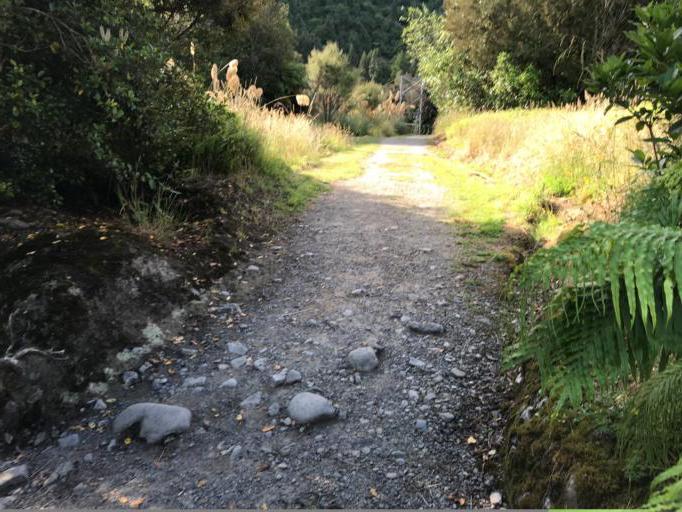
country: NZ
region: Wellington
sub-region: Kapiti Coast District
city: Otaki
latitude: -40.8725
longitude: 175.2315
